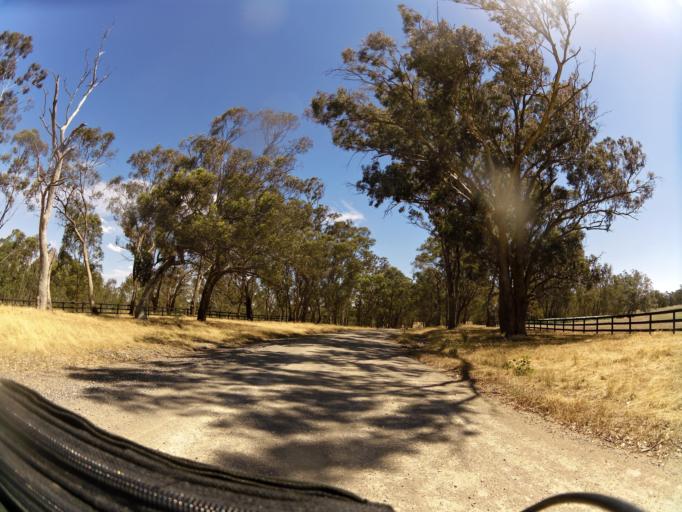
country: AU
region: Victoria
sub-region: Campaspe
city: Kyabram
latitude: -36.8289
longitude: 145.0775
